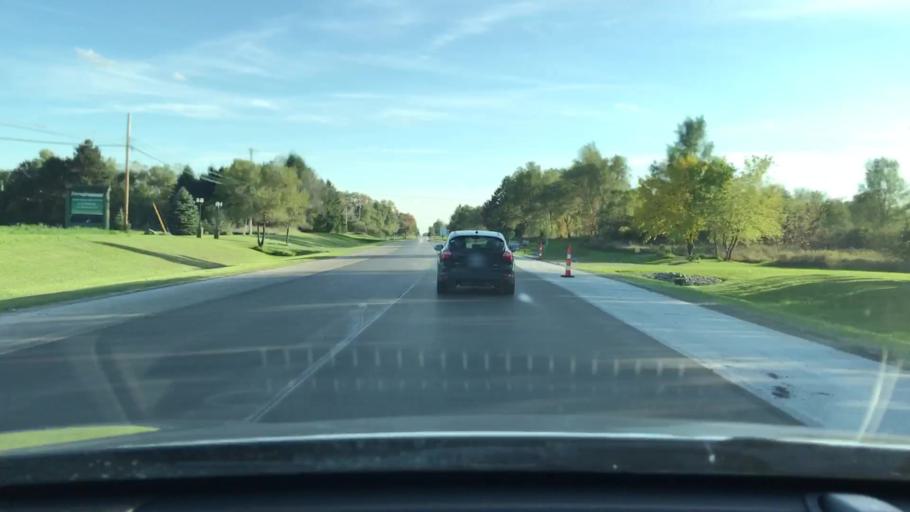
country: US
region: Michigan
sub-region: Shiawassee County
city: Owosso
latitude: 42.9408
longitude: -84.2227
